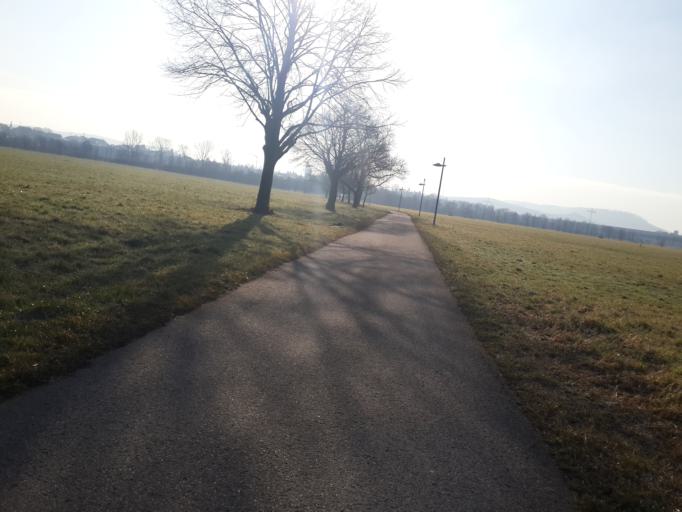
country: DE
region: Baden-Wuerttemberg
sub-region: Regierungsbezirk Stuttgart
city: Neckarsulm
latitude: 49.1918
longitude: 9.2099
